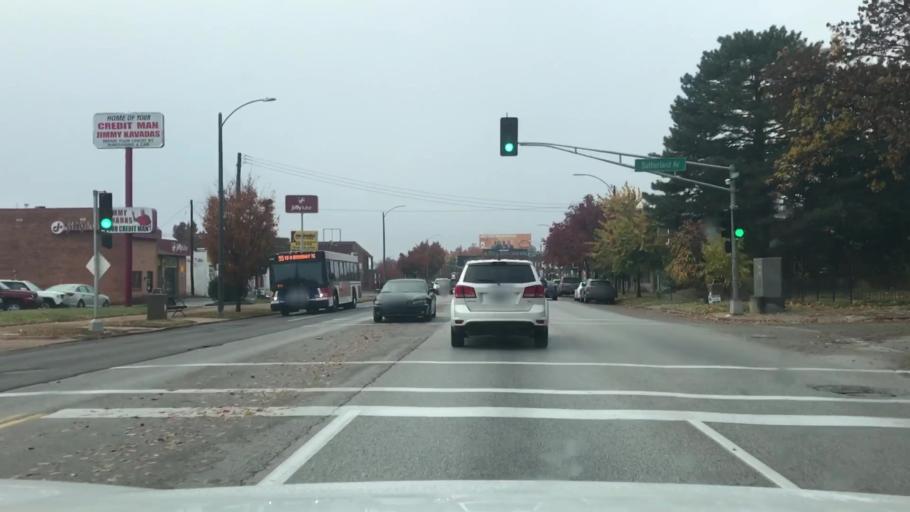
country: US
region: Missouri
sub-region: Saint Louis County
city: Maplewood
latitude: 38.5887
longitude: -90.2753
